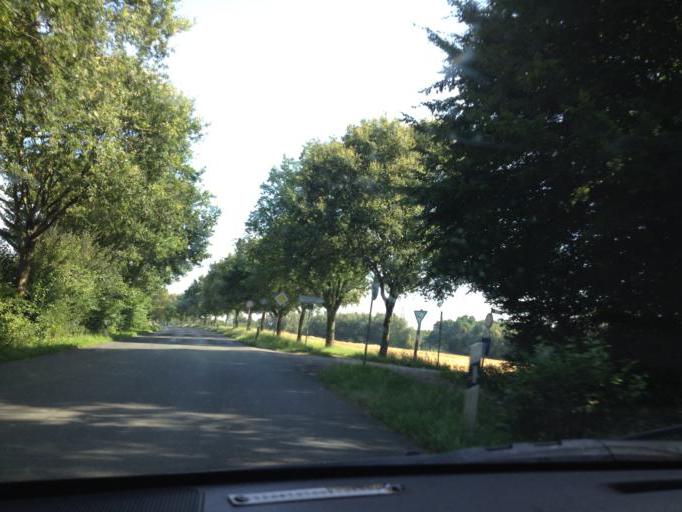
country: DE
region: North Rhine-Westphalia
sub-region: Regierungsbezirk Arnsberg
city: Holzwickede
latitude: 51.5150
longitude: 7.6372
